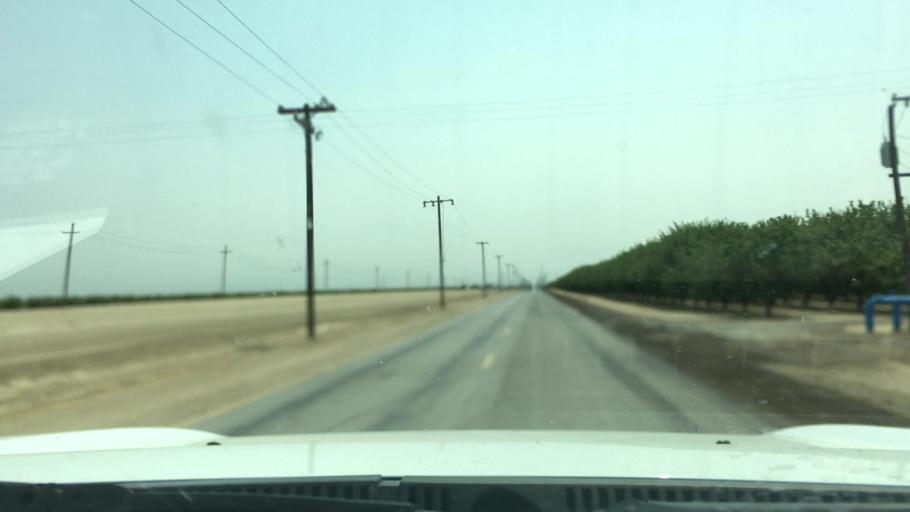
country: US
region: California
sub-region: Kern County
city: Wasco
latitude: 35.6235
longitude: -119.4378
